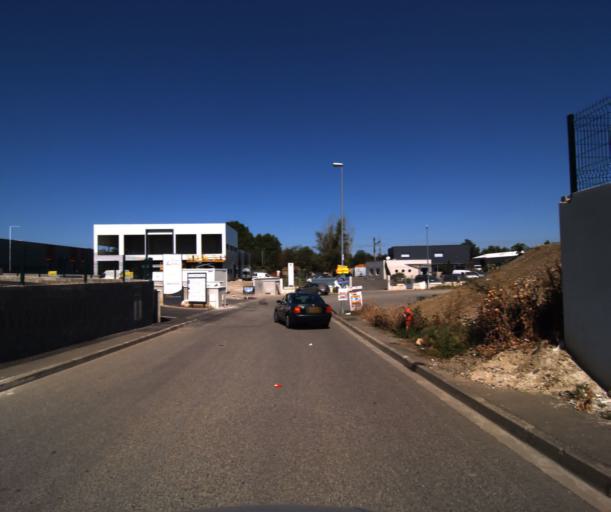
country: FR
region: Midi-Pyrenees
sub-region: Departement de la Haute-Garonne
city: Saubens
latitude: 43.4771
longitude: 1.3321
